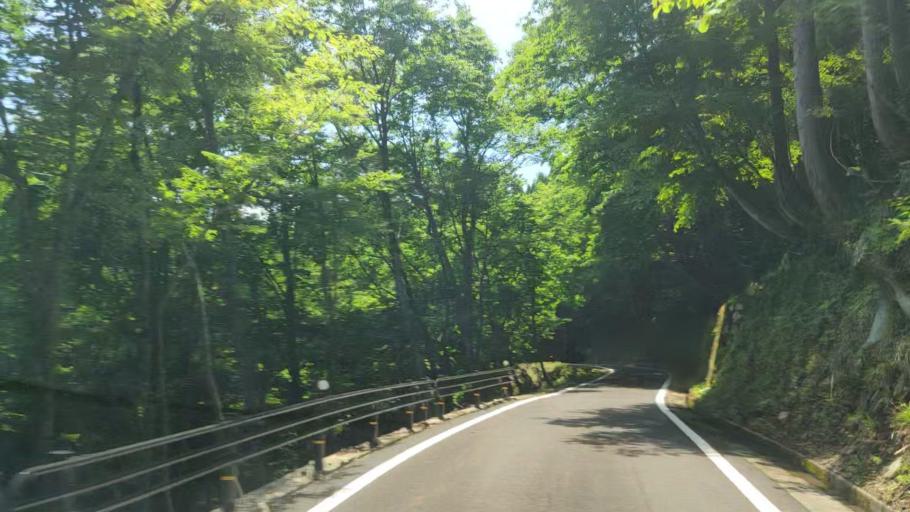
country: JP
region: Tottori
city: Tottori
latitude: 35.3763
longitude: 134.4904
